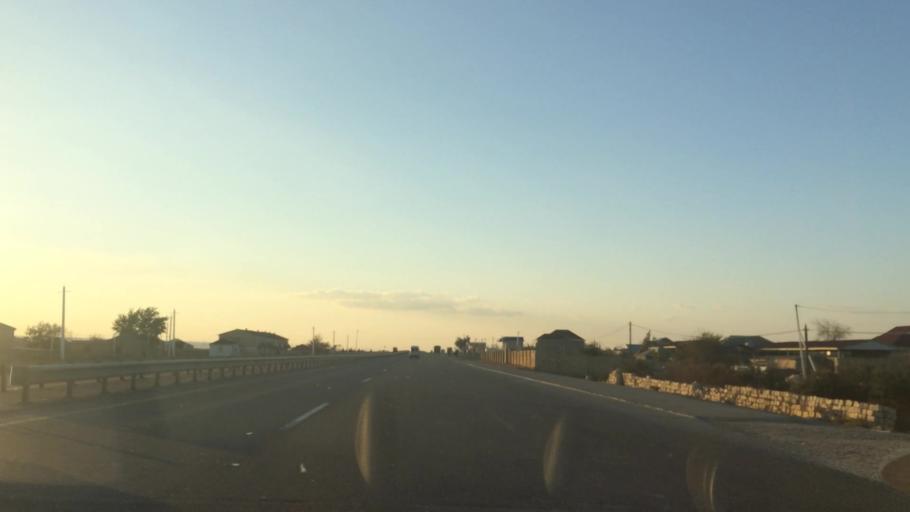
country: AZ
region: Baki
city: Qobustan
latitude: 39.9718
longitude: 49.2606
